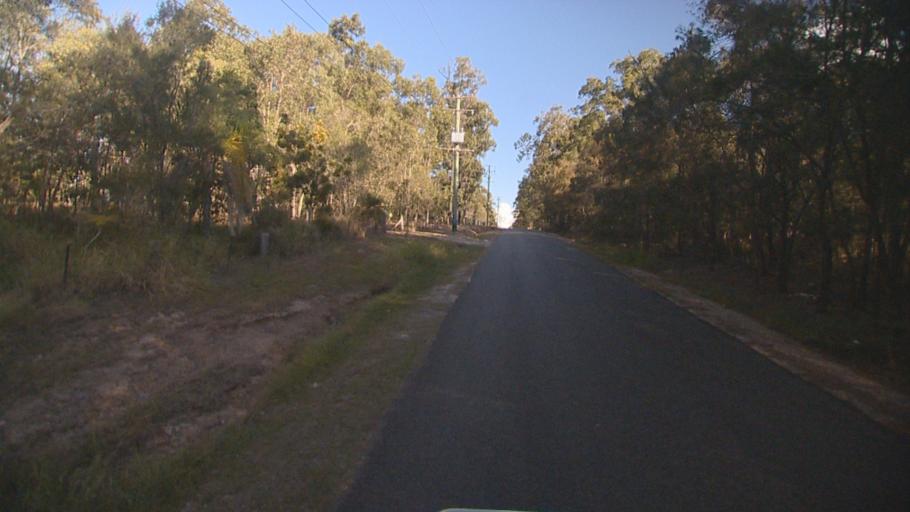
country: AU
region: Queensland
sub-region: Ipswich
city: Springfield Lakes
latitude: -27.7009
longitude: 152.9484
